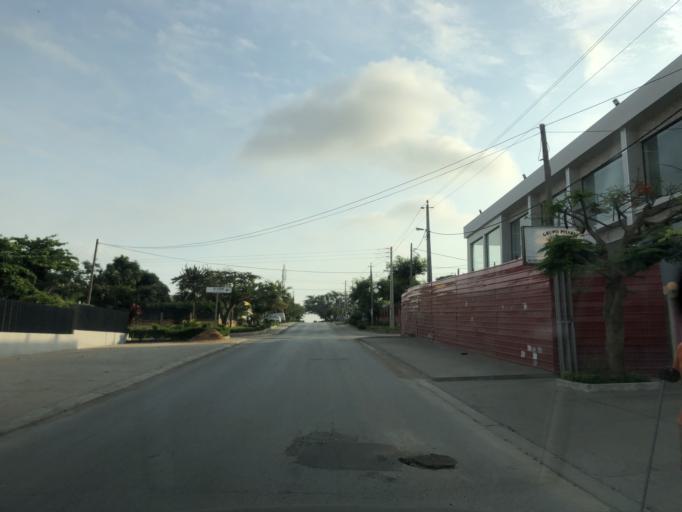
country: AO
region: Luanda
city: Luanda
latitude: -8.9009
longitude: 13.2264
